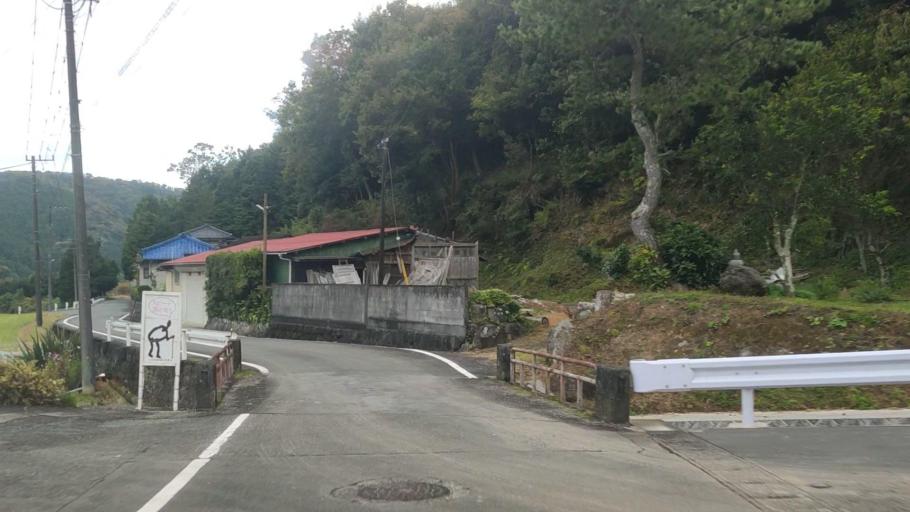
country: JP
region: Shizuoka
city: Ito
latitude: 34.9336
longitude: 139.0030
